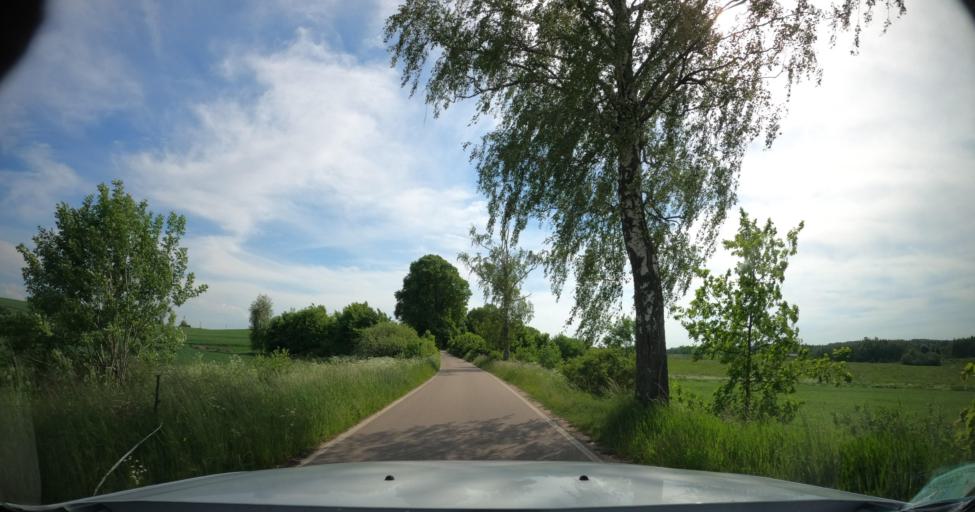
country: PL
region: Warmian-Masurian Voivodeship
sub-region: Powiat ostrodzki
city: Milakowo
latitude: 54.0187
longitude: 20.1584
